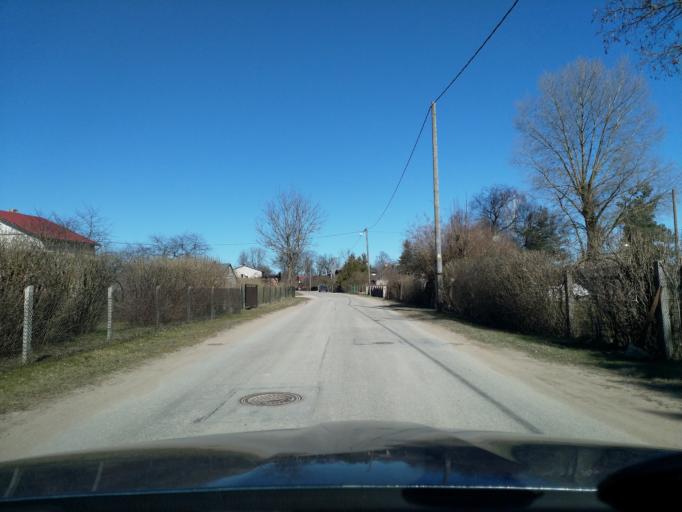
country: LV
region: Kuldigas Rajons
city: Kuldiga
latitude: 56.9626
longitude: 21.9989
